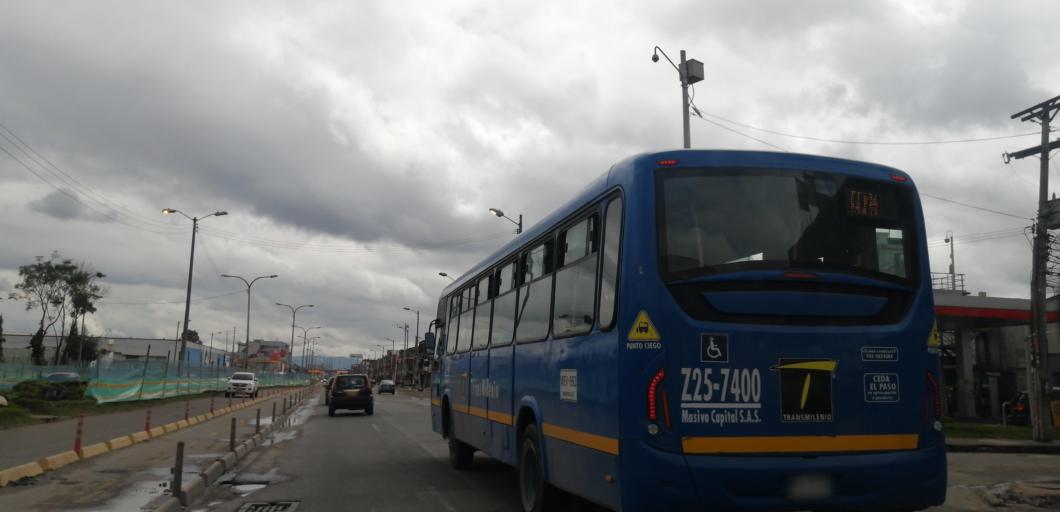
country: CO
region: Bogota D.C.
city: Bogota
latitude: 4.6017
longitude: -74.1337
